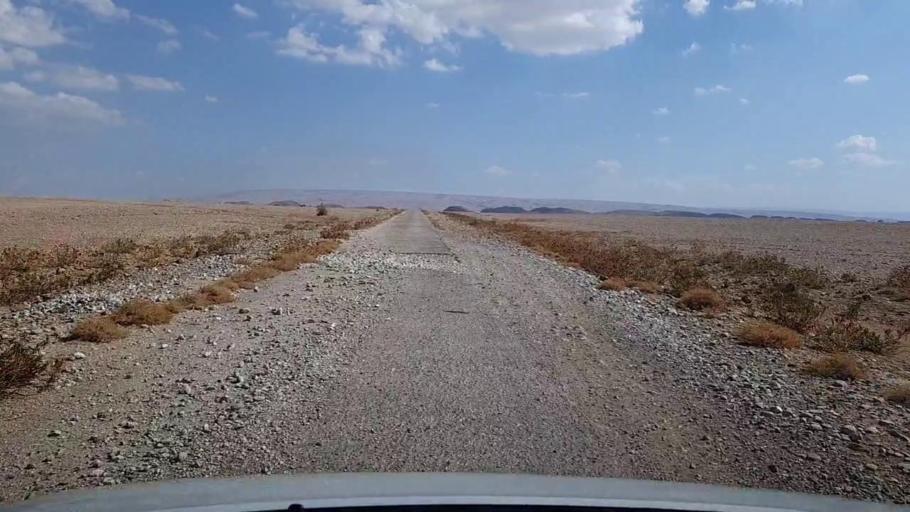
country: PK
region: Sindh
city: Bhan
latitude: 26.3714
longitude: 67.6412
